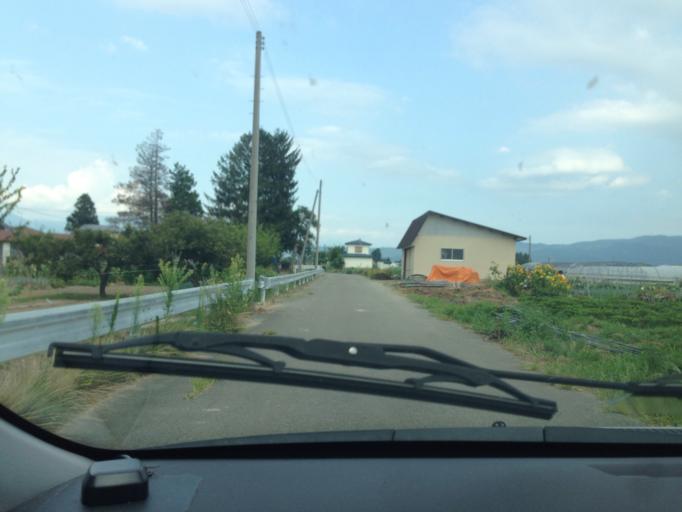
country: JP
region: Fukushima
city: Kitakata
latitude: 37.5020
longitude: 139.8655
